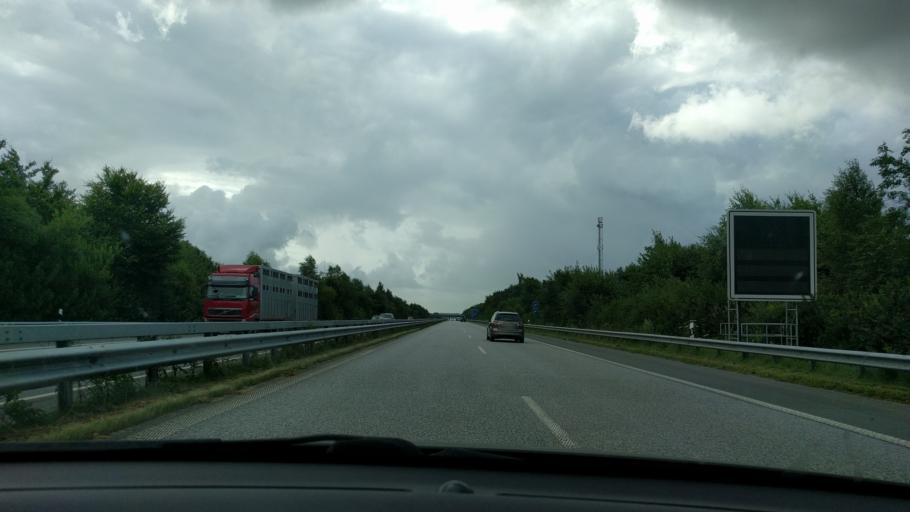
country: DE
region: Schleswig-Holstein
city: Tensbuttel-Rost
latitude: 54.1243
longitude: 9.2563
